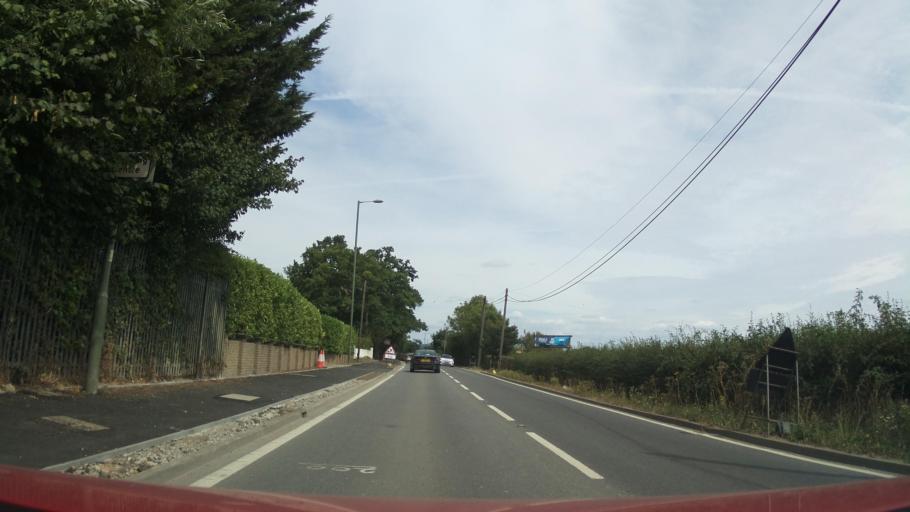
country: GB
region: England
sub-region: Surrey
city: Salfords
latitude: 51.1866
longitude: -0.1959
